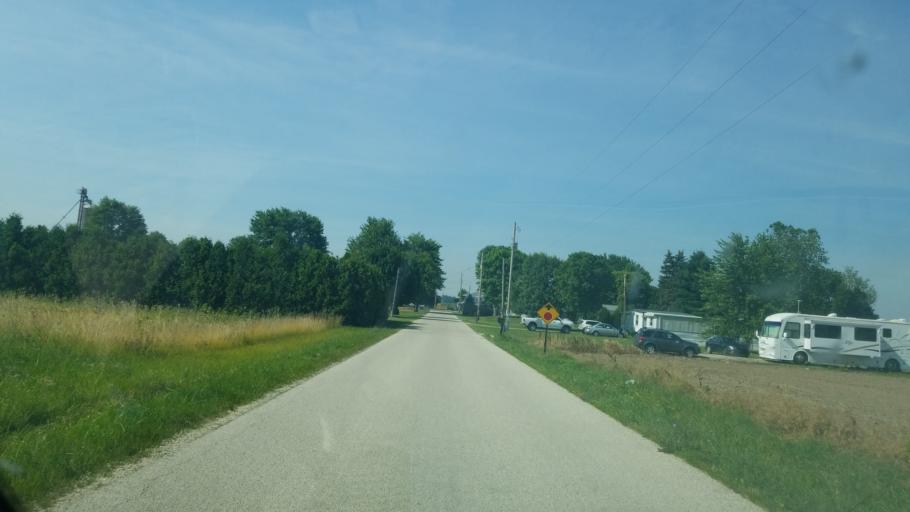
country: US
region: Ohio
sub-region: Wyandot County
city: Carey
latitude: 41.0046
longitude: -83.3253
